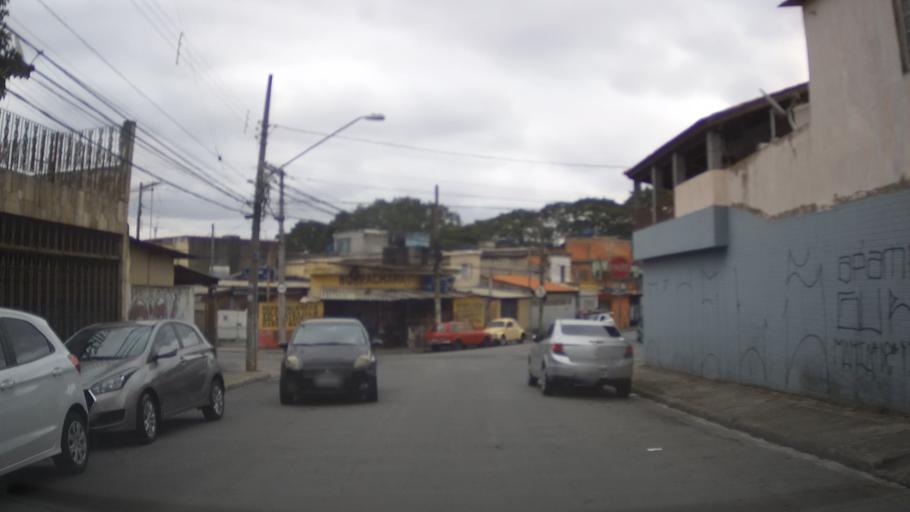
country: BR
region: Sao Paulo
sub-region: Guarulhos
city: Guarulhos
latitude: -23.4498
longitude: -46.5062
